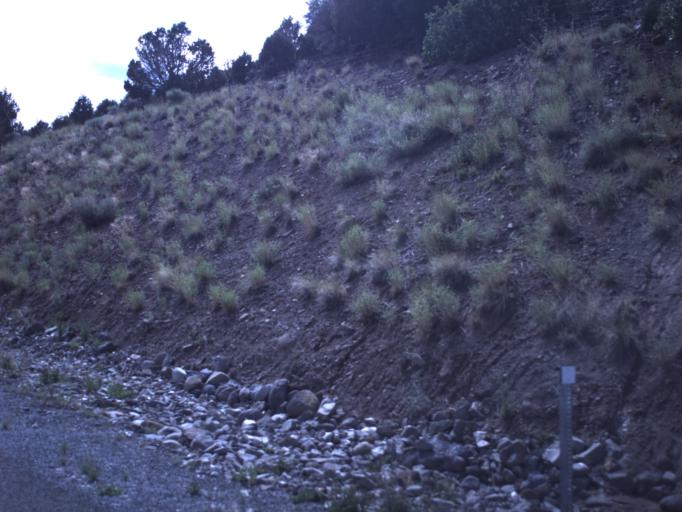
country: US
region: Utah
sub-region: Garfield County
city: Panguitch
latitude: 38.0250
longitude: -112.5191
